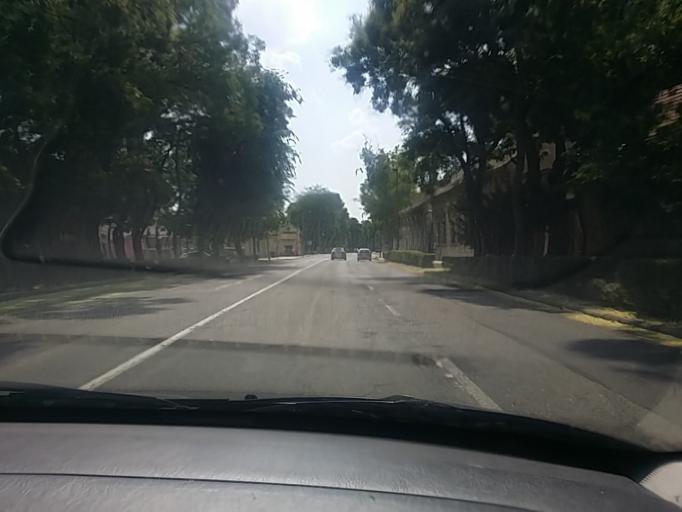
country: HU
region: Tolna
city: Dombovar
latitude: 46.3716
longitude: 18.1297
